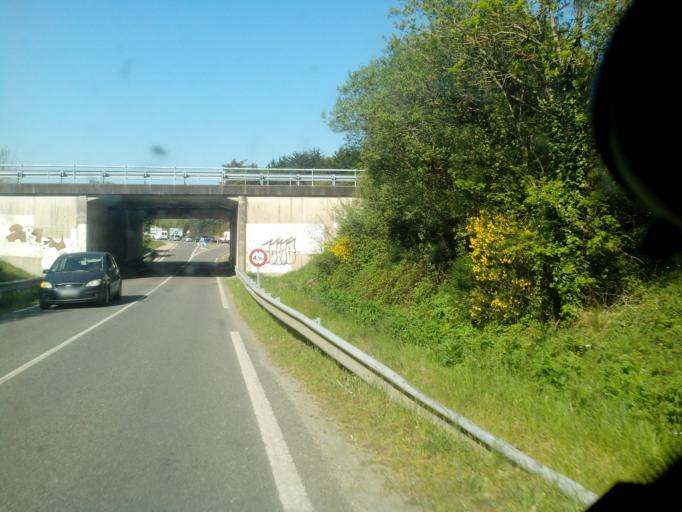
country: FR
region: Pays de la Loire
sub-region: Departement de la Loire-Atlantique
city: Pornic
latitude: 47.1104
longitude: -2.0745
